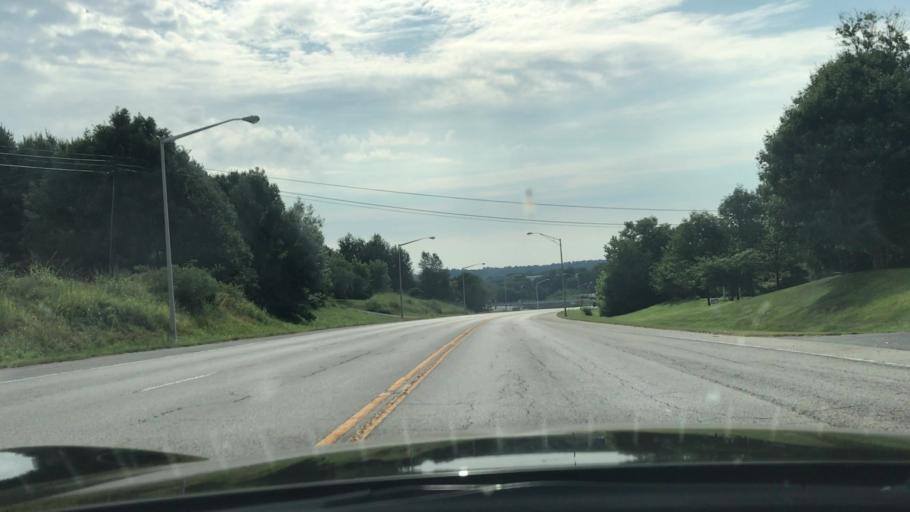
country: US
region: Kentucky
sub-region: Green County
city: Greensburg
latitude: 37.2726
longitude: -85.5015
